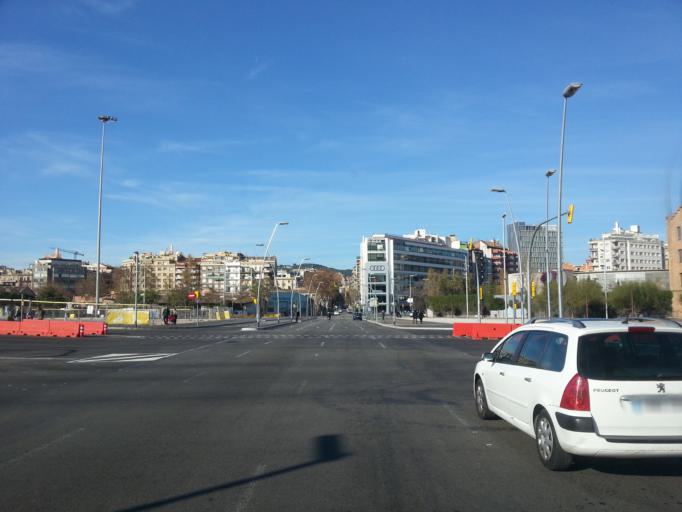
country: ES
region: Catalonia
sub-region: Provincia de Barcelona
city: Sant Marti
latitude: 41.4041
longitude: 2.1882
